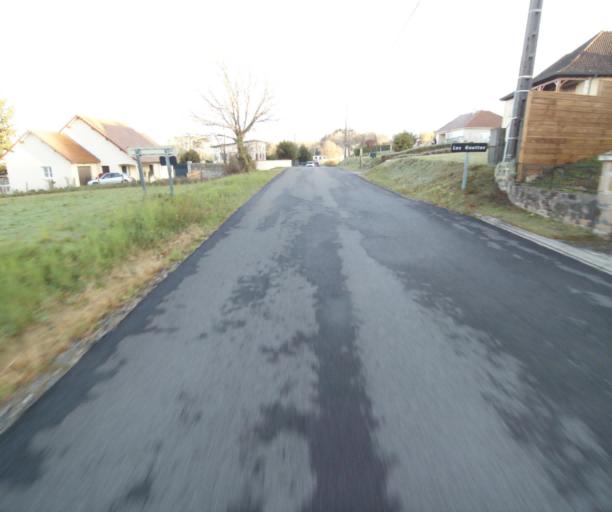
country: FR
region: Limousin
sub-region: Departement de la Correze
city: Correze
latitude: 45.3157
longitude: 1.8426
